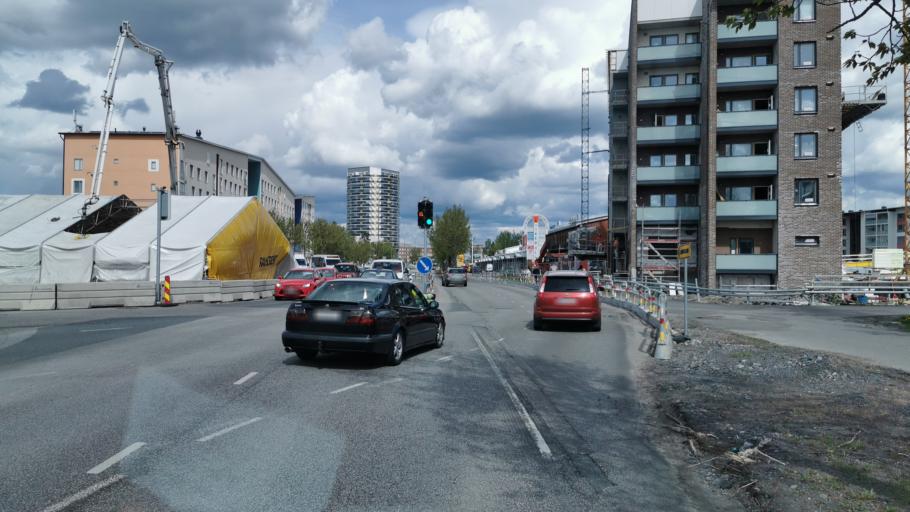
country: FI
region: Northern Ostrobothnia
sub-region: Oulu
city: Oulu
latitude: 65.0004
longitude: 25.4640
